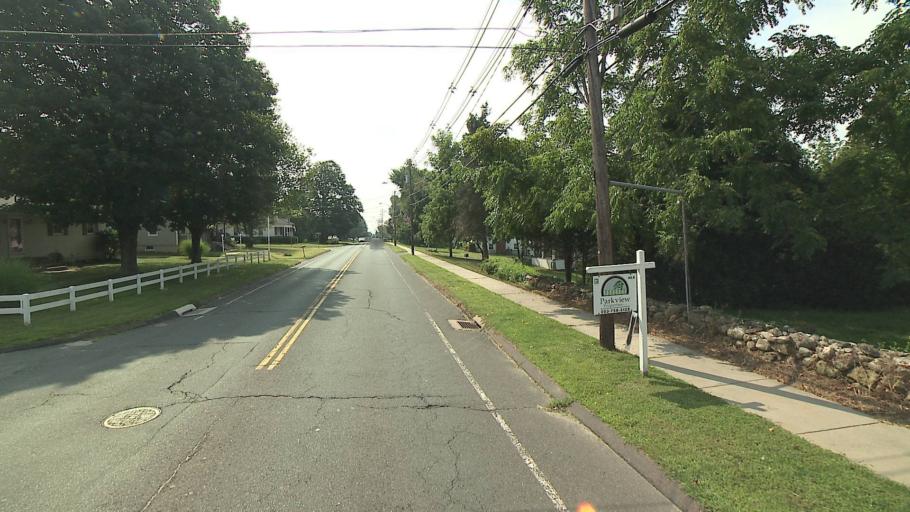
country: US
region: Connecticut
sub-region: Litchfield County
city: Oakville
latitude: 41.6061
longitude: -73.0900
